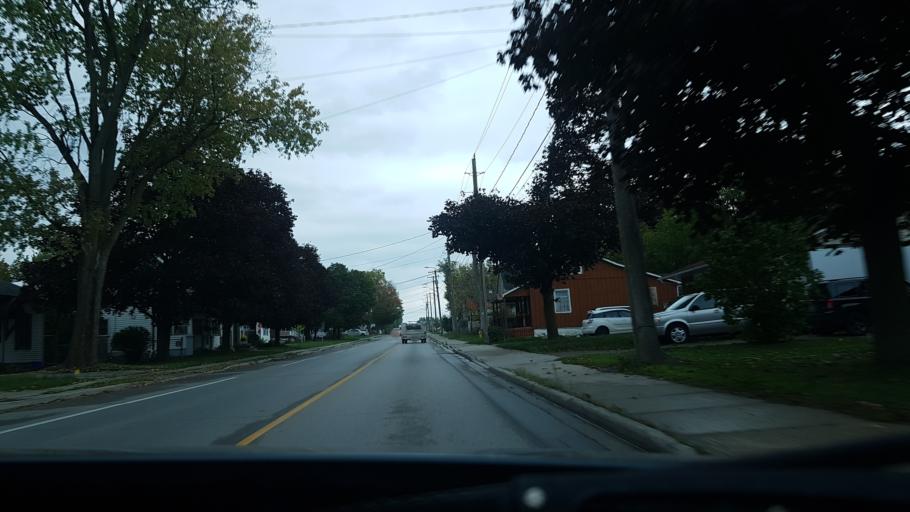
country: CA
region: Ontario
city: Omemee
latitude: 44.3591
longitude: -78.7303
